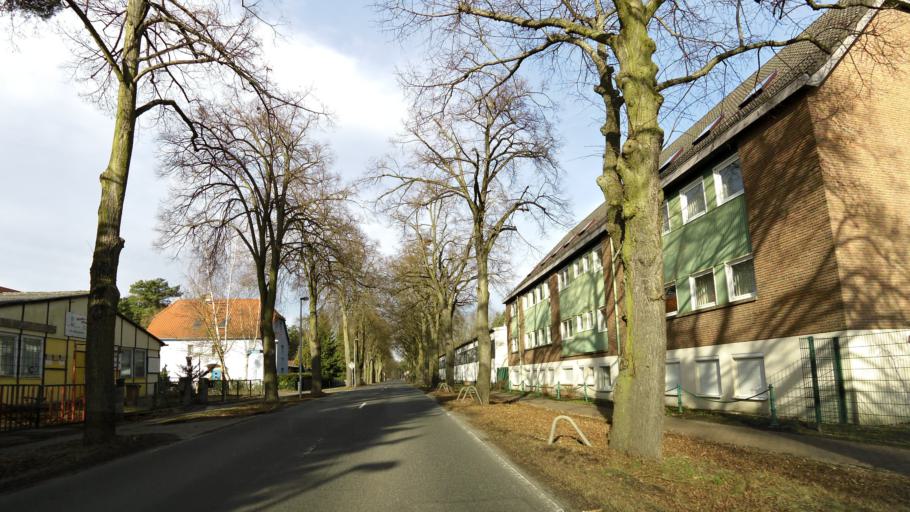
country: DE
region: Brandenburg
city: Michendorf
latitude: 52.3248
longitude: 13.0296
